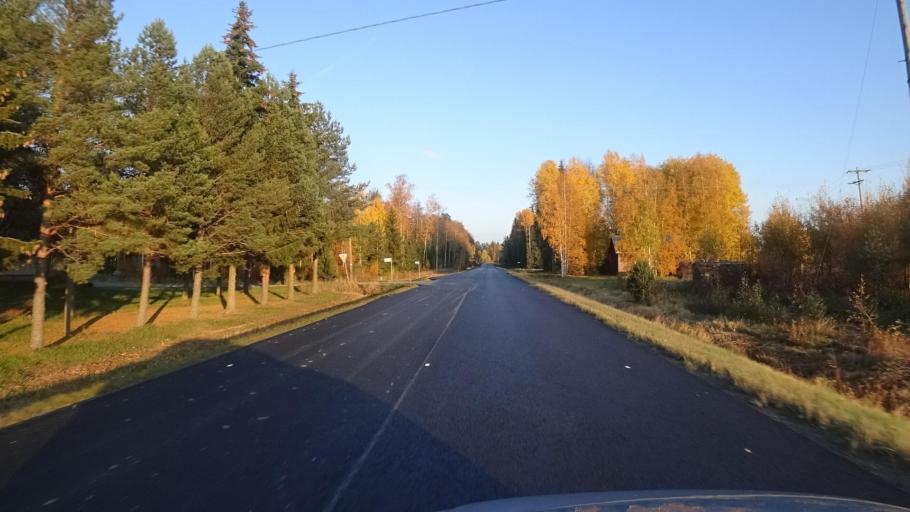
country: FI
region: Haeme
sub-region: Forssa
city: Ypaejae
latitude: 60.7758
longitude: 23.3295
